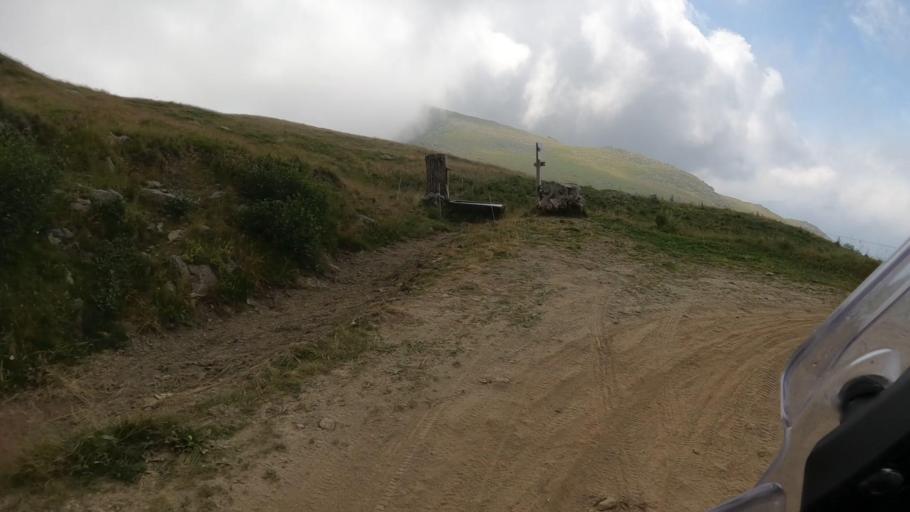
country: IT
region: Piedmont
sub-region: Provincia di Torino
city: Lemie
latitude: 45.1706
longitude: 7.2798
